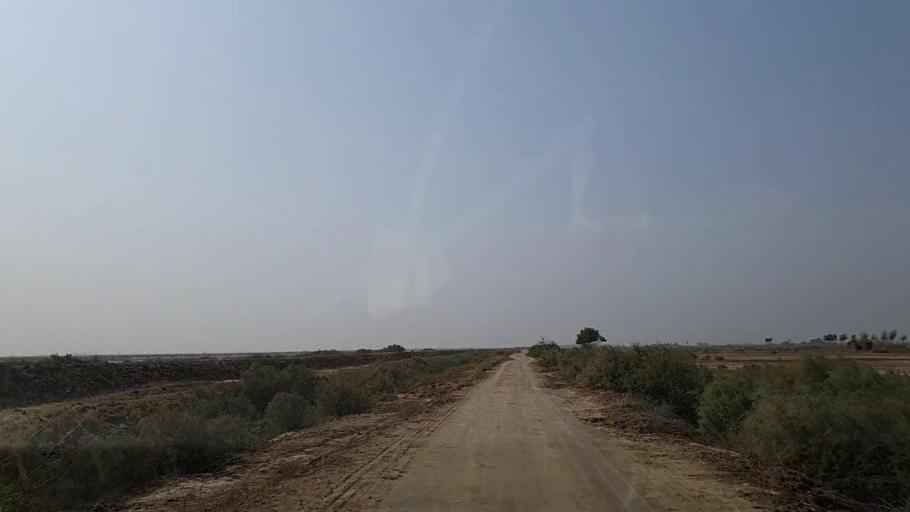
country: PK
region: Sindh
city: Gharo
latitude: 24.6738
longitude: 67.7218
